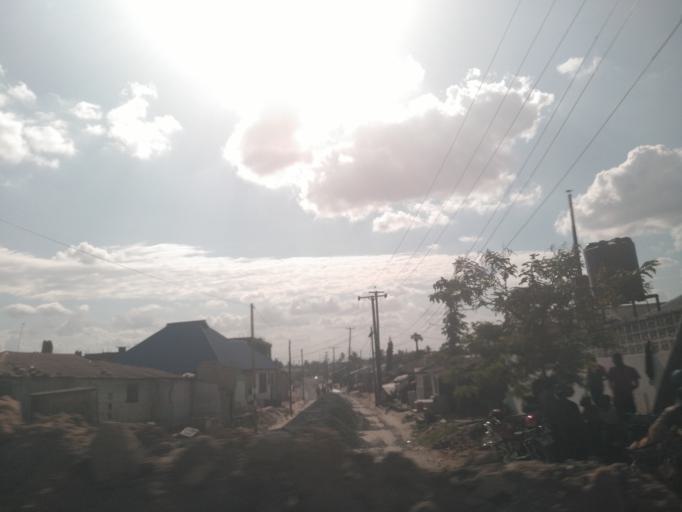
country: TZ
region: Dar es Salaam
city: Dar es Salaam
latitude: -6.8684
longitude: 39.2559
